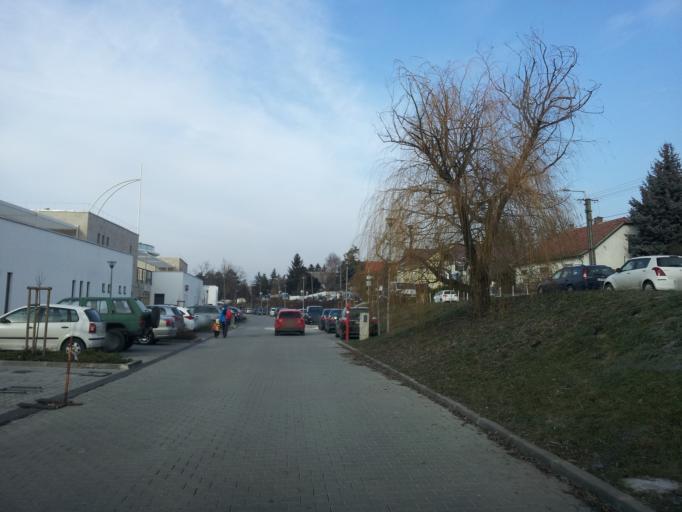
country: HU
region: Fejer
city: Velence
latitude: 47.2328
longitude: 18.6621
